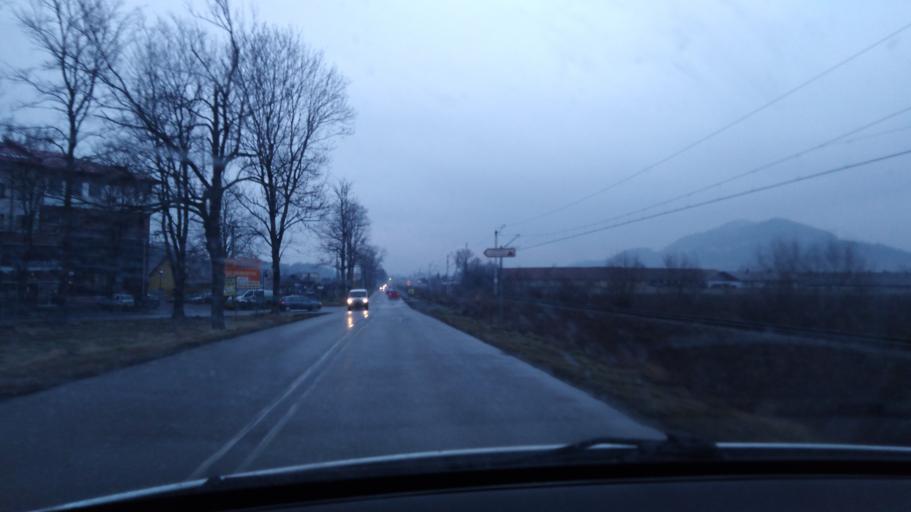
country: PL
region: Silesian Voivodeship
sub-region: Powiat zywiecki
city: Wieprz
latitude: 49.6439
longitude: 19.1611
